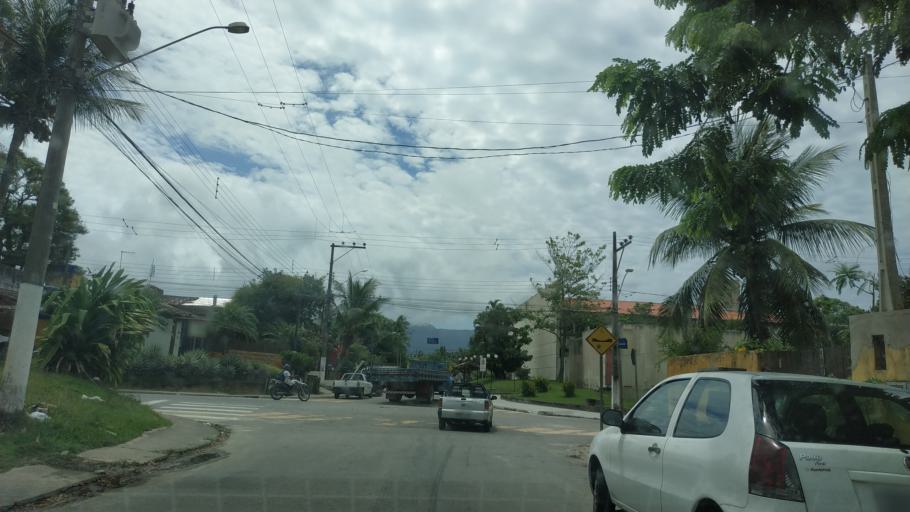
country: BR
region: Sao Paulo
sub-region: Ilhabela
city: Ilhabela
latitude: -23.8211
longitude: -45.3687
